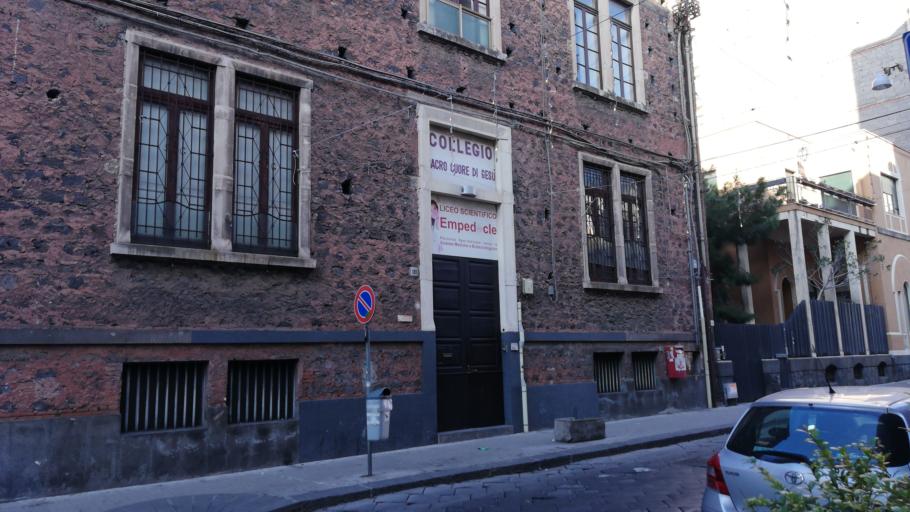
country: IT
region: Sicily
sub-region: Catania
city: Canalicchio
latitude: 37.5175
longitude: 15.0983
